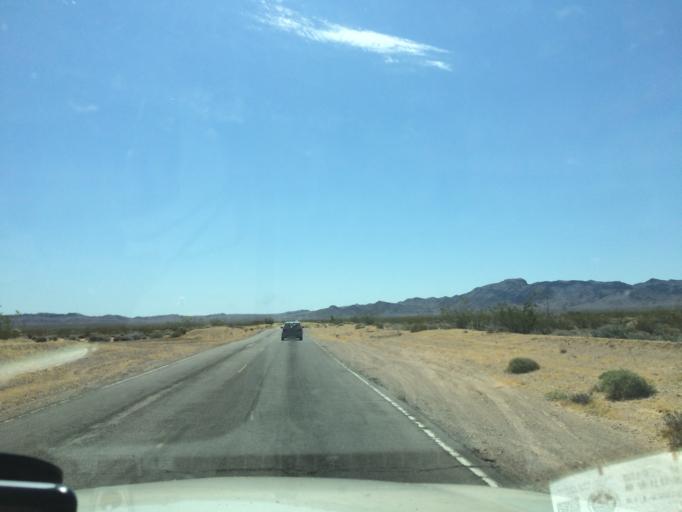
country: US
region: Nevada
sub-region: Clark County
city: Moapa Town
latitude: 36.4577
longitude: -114.7267
